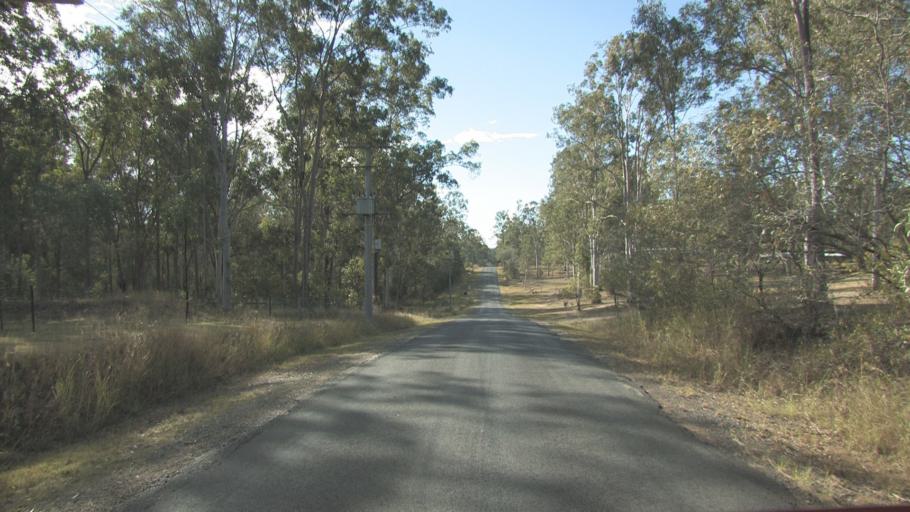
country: AU
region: Queensland
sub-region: Logan
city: Cedar Vale
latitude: -27.8299
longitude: 153.0618
